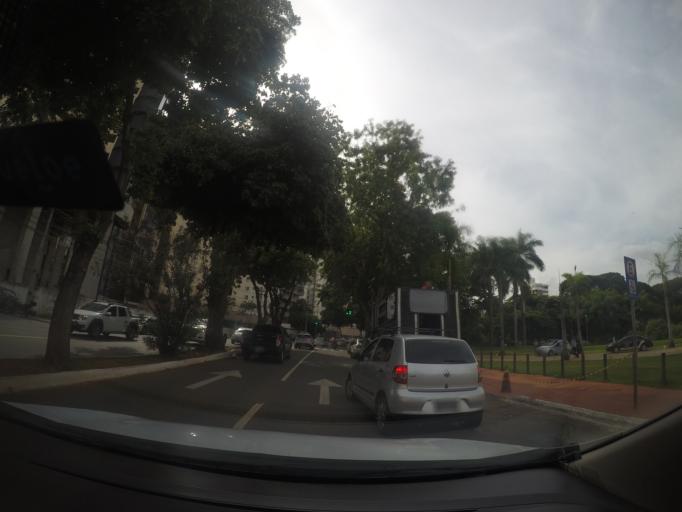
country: BR
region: Goias
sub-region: Goiania
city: Goiania
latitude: -16.6794
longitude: -49.2610
